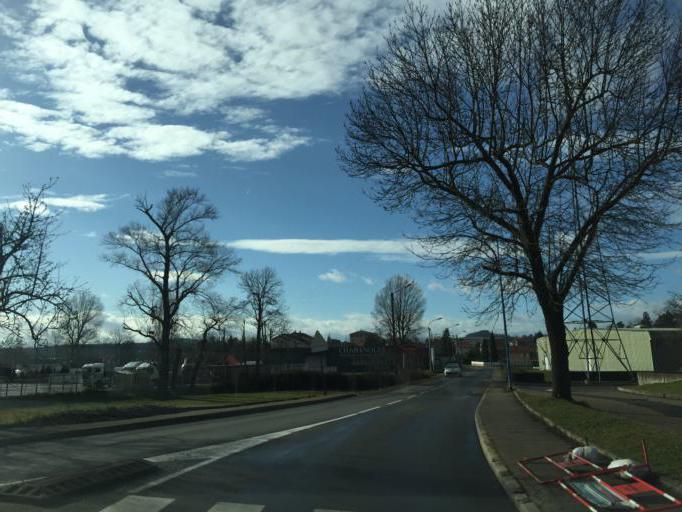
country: FR
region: Rhone-Alpes
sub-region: Departement de la Loire
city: La Talaudiere
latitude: 45.4781
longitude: 4.4431
